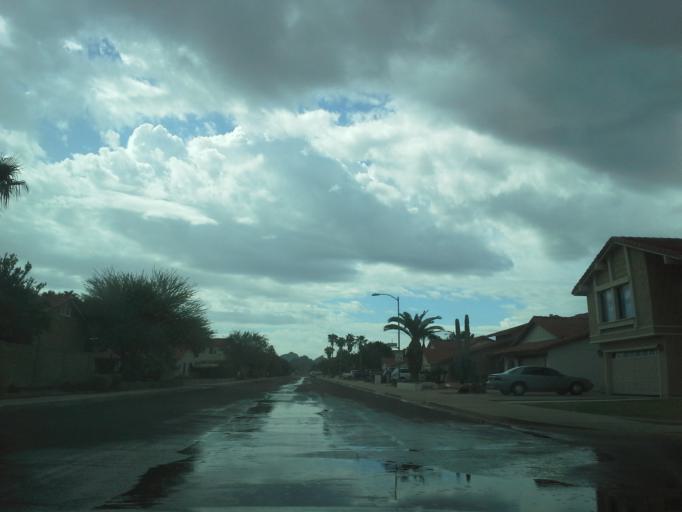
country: US
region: Arizona
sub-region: Maricopa County
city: Paradise Valley
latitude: 33.6142
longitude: -112.0395
